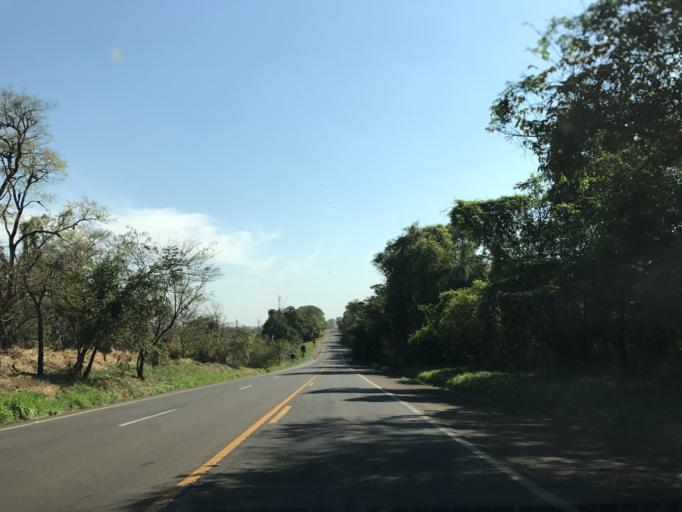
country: BR
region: Sao Paulo
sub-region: Jose Bonifacio
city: Jose Bonifacio
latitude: -21.0705
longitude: -49.7496
